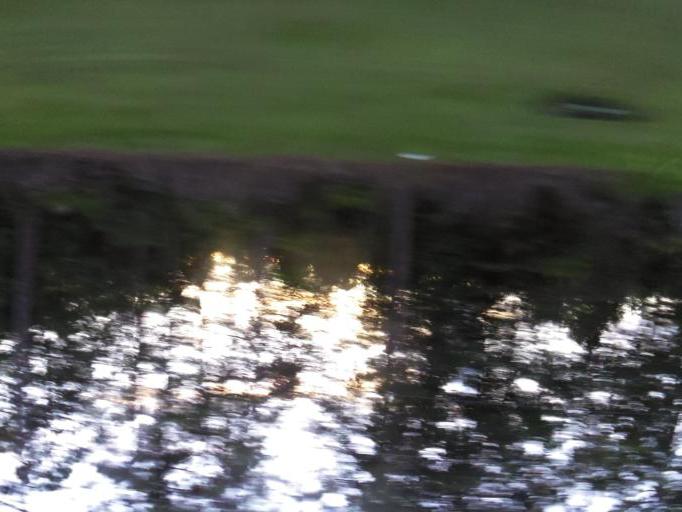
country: US
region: Georgia
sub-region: Camden County
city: Kingsland
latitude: 30.7666
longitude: -81.6872
